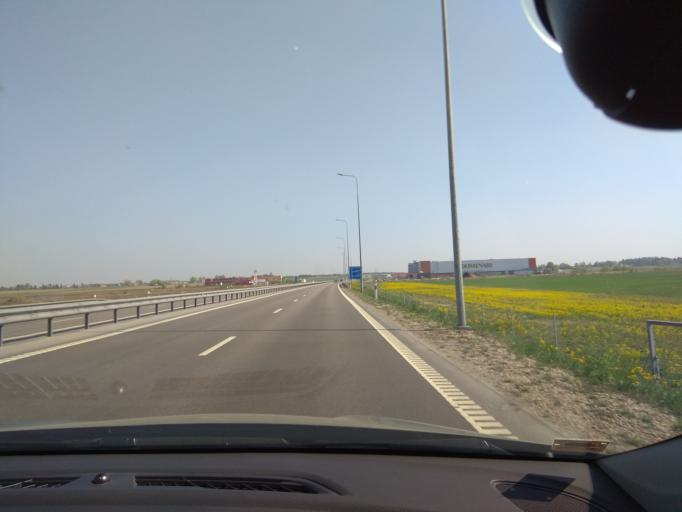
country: LT
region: Panevezys
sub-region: Panevezys City
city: Panevezys
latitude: 55.6721
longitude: 24.3404
